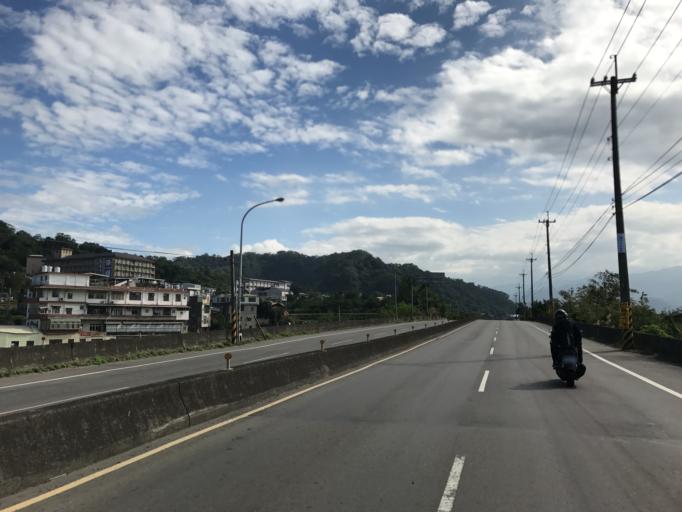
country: TW
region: Taiwan
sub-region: Hsinchu
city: Zhubei
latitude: 24.7476
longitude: 121.0989
